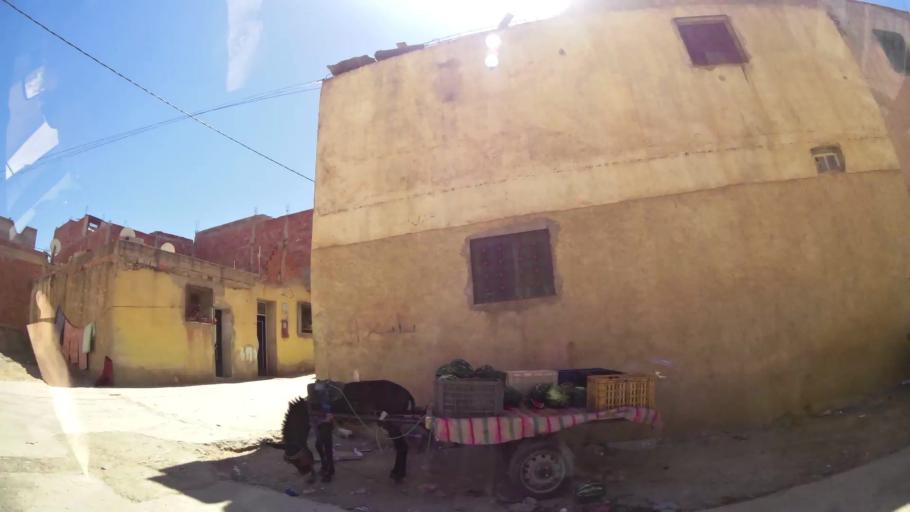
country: MA
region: Oriental
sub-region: Oujda-Angad
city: Oujda
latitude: 34.6545
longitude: -1.8648
